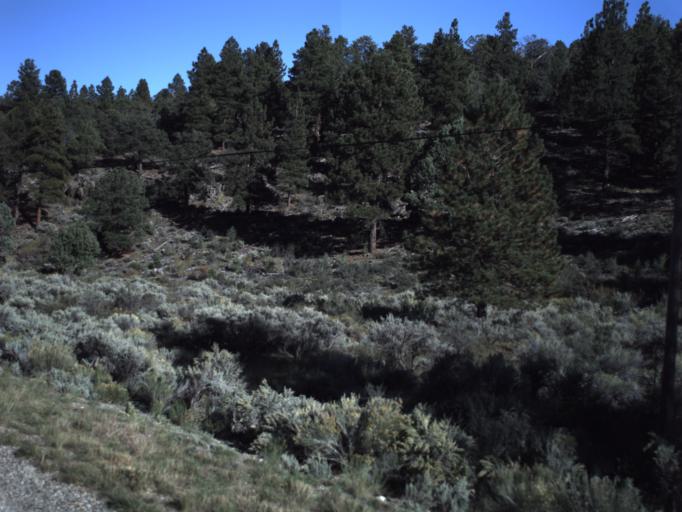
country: US
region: Utah
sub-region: Garfield County
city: Panguitch
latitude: 37.7666
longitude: -112.4591
